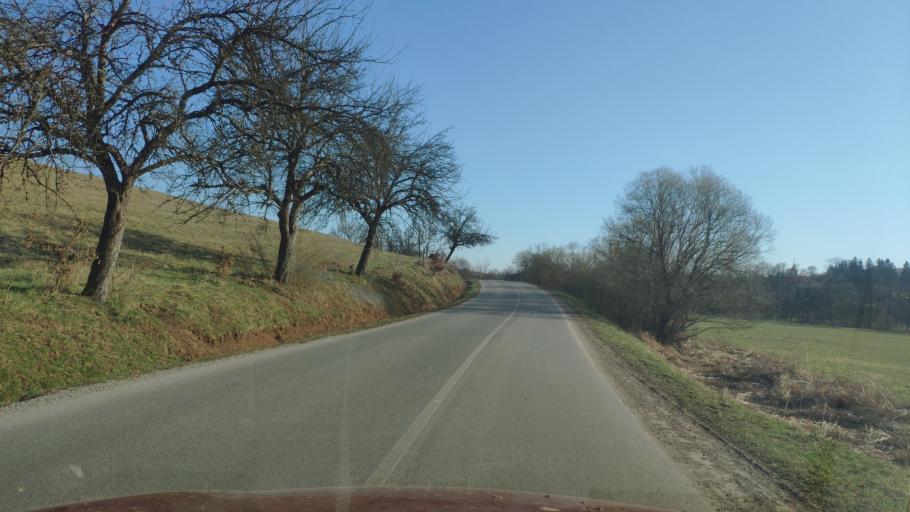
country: SK
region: Banskobystricky
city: Revuca
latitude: 48.5178
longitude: 20.2560
